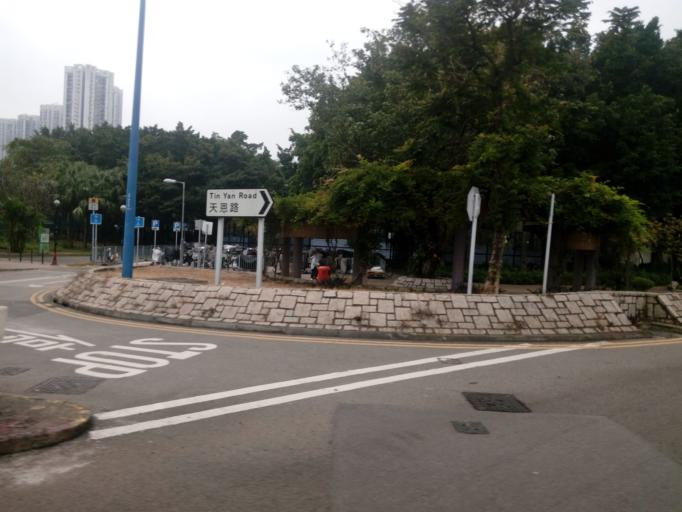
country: HK
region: Yuen Long
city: Yuen Long Kau Hui
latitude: 22.4563
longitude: 114.0059
